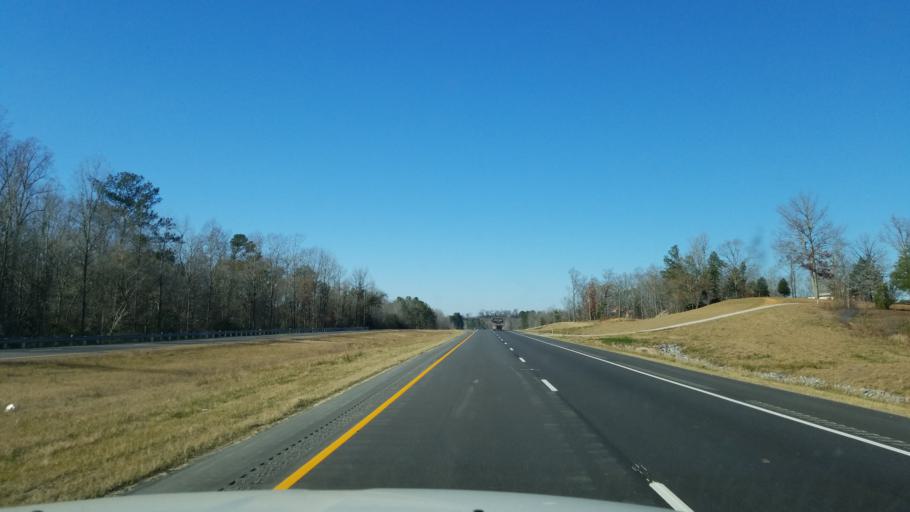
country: US
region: Alabama
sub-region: Pickens County
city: Reform
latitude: 33.3636
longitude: -87.9779
